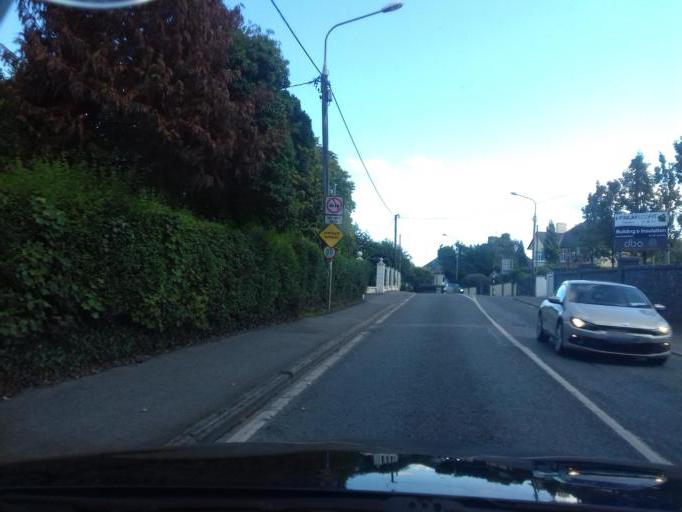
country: IE
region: Leinster
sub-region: Uibh Fhaili
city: Tullamore
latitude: 53.2694
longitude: -7.4903
